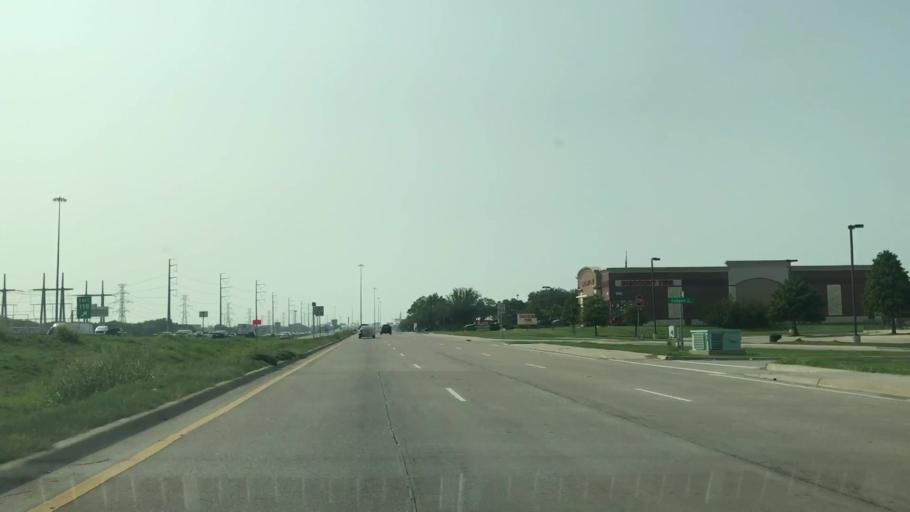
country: US
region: Texas
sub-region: Dallas County
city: Garland
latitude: 32.8572
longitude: -96.6496
